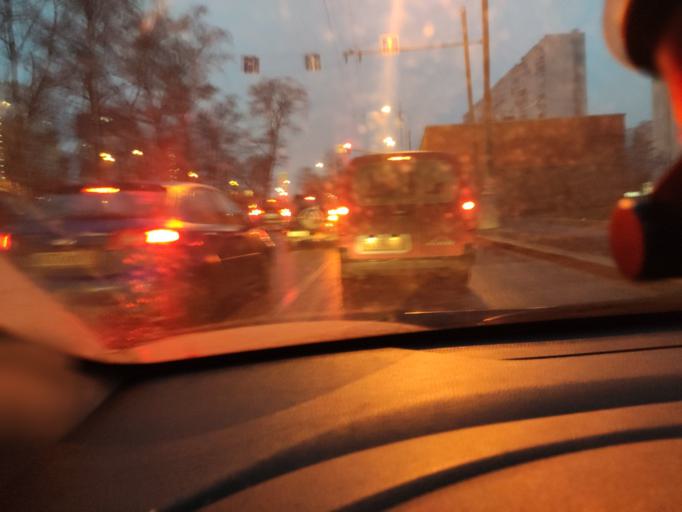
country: RU
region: Moscow
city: Chertanovo Yuzhnoye
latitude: 55.5930
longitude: 37.5997
